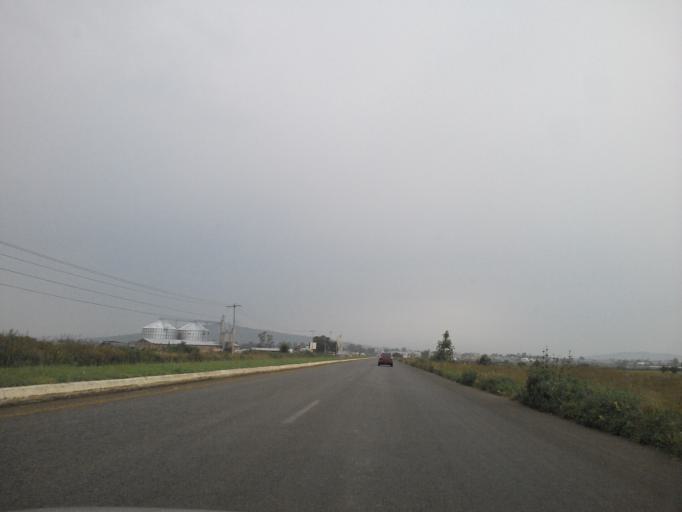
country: MX
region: Jalisco
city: Capilla de Guadalupe
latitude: 20.8075
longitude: -102.5774
